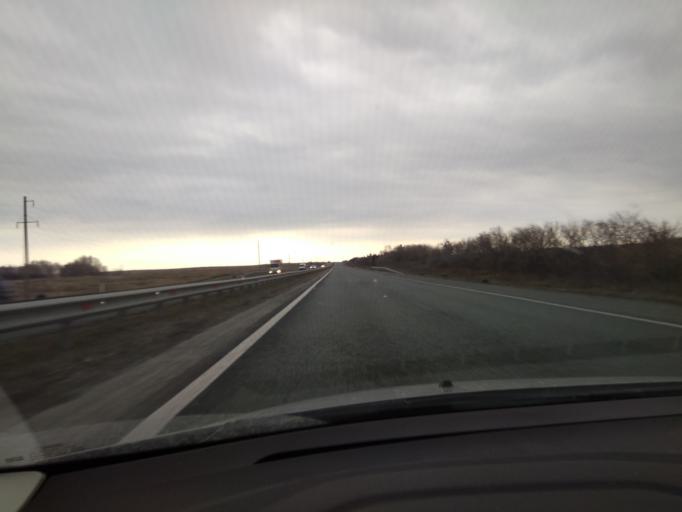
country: RU
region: Chelyabinsk
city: Tyubuk
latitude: 55.8085
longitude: 61.1978
